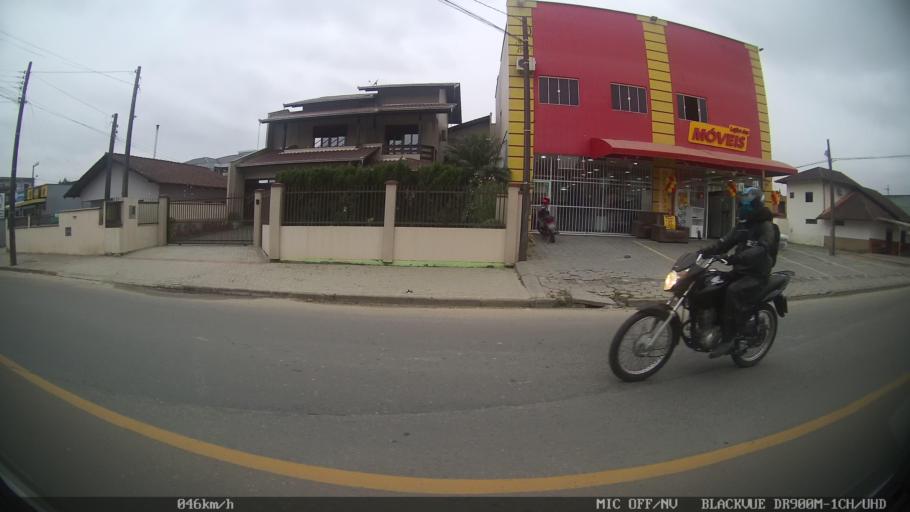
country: BR
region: Santa Catarina
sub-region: Joinville
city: Joinville
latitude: -26.3661
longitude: -48.8295
